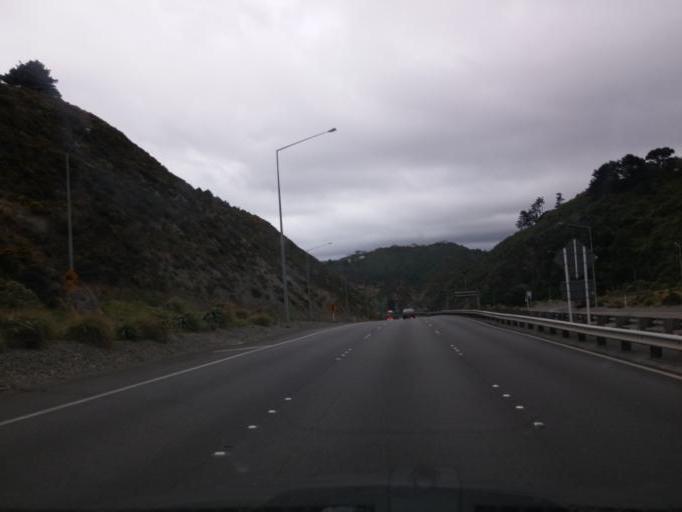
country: NZ
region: Wellington
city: Petone
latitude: -41.2320
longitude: 174.8096
